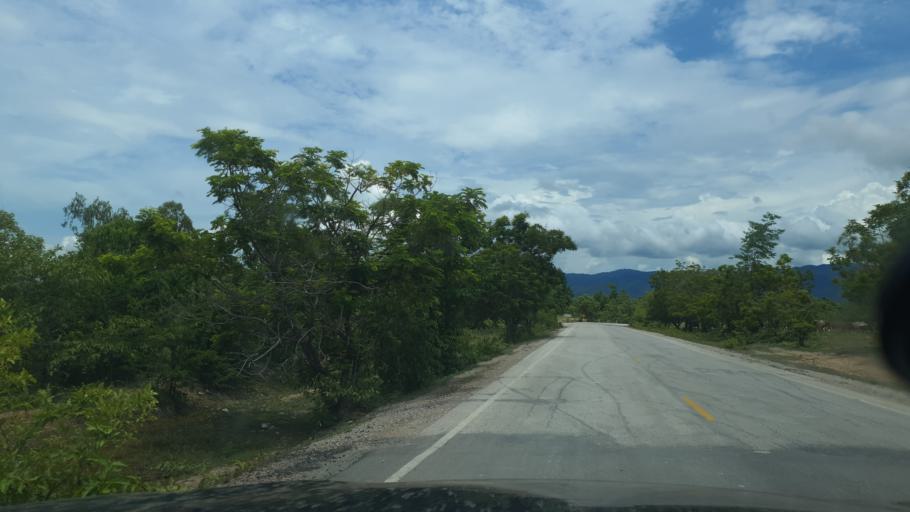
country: TH
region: Lampang
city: Sop Prap
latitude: 17.9336
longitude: 99.3668
